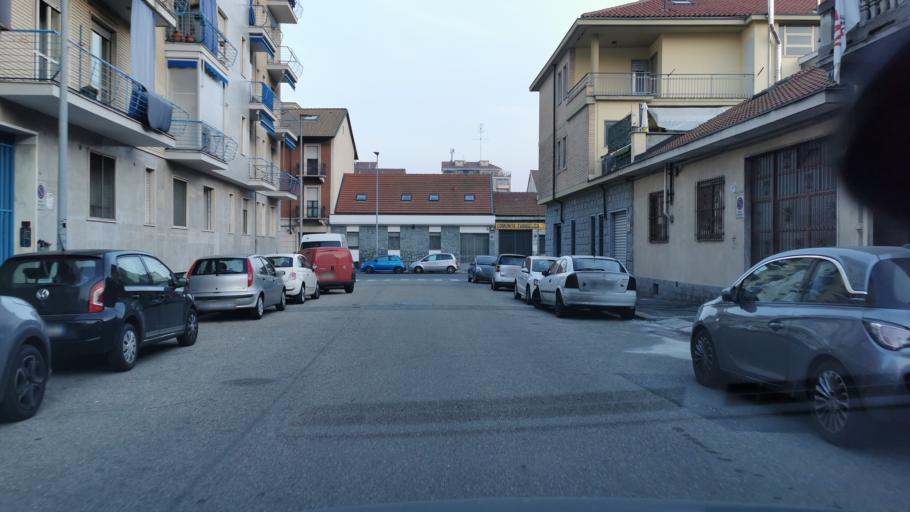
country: IT
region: Piedmont
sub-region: Provincia di Torino
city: Venaria Reale
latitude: 45.1006
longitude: 7.6575
